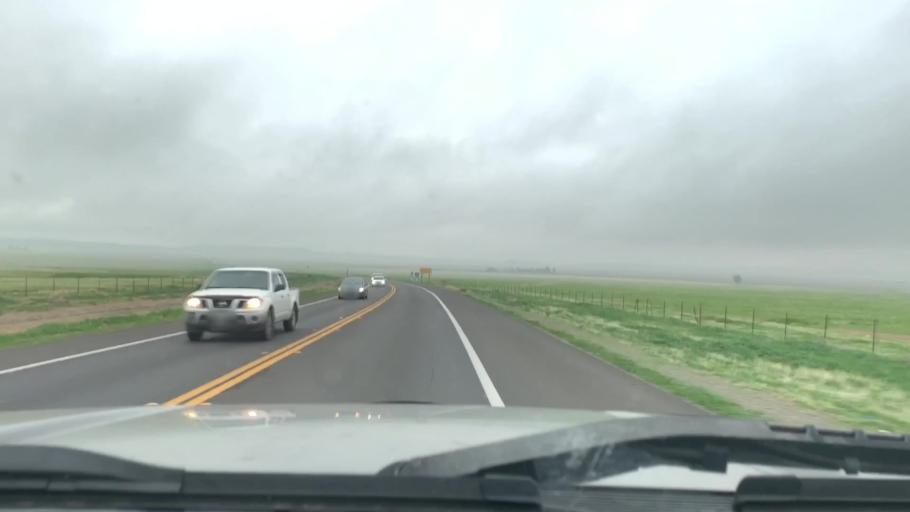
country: US
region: California
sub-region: Kings County
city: Avenal
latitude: 35.7878
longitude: -120.1134
